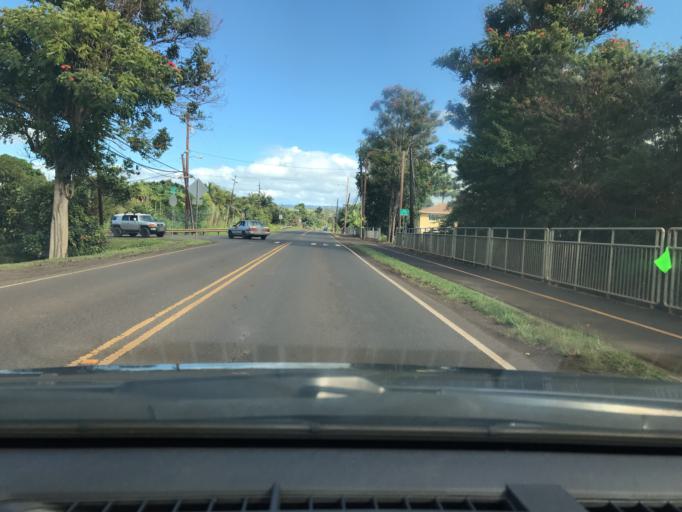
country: US
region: Hawaii
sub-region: Honolulu County
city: Waialua
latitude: 21.5757
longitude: -158.1174
